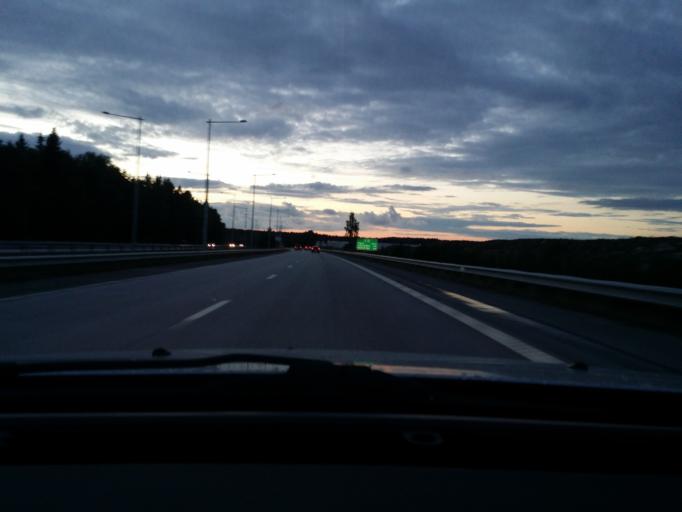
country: SE
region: Stockholm
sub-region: Upplands-Bro Kommun
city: Kungsaengen
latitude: 59.5030
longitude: 17.7353
